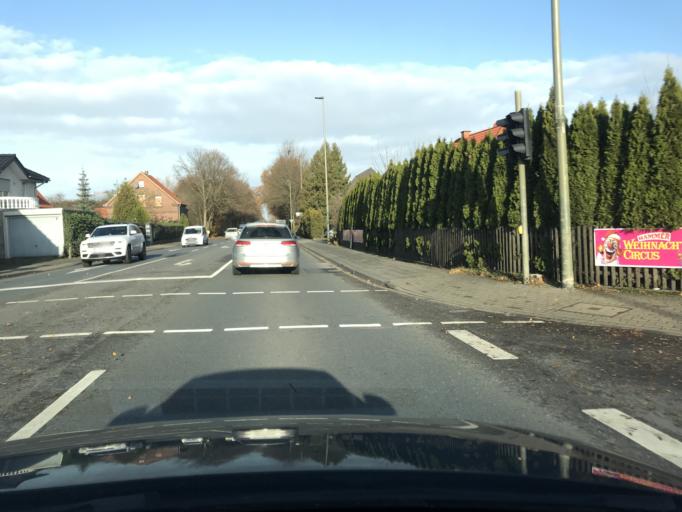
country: DE
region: North Rhine-Westphalia
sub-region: Regierungsbezirk Arnsberg
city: Hamm
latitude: 51.6496
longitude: 7.8411
